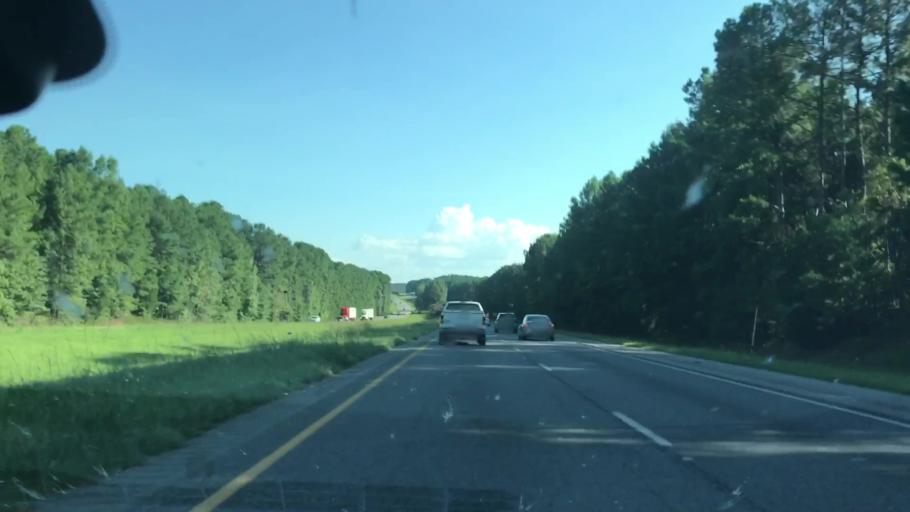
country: US
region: Georgia
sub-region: Harris County
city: Hamilton
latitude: 32.8023
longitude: -85.0215
